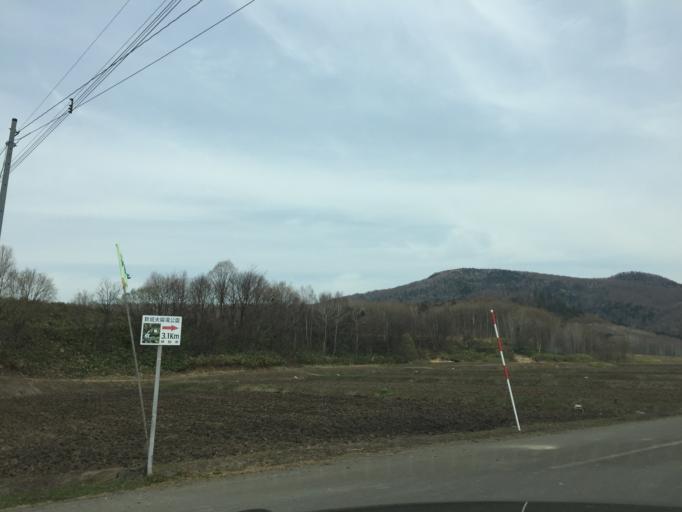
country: JP
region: Hokkaido
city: Ashibetsu
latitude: 43.6192
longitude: 142.2145
